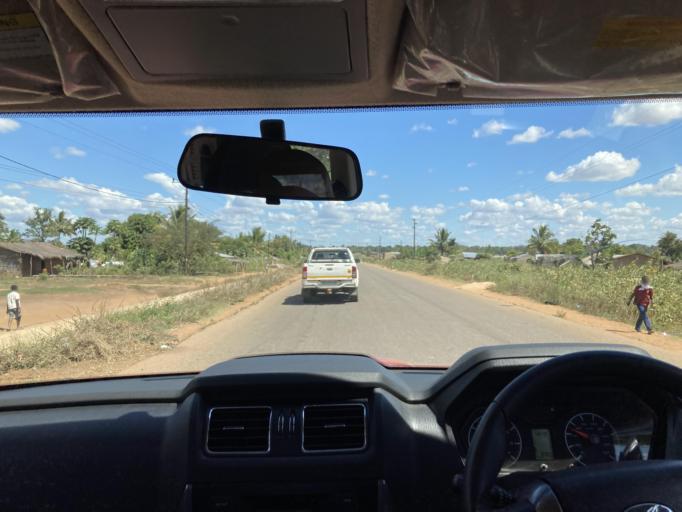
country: MZ
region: Cabo Delgado
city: Montepuez
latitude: -13.1349
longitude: 38.9905
